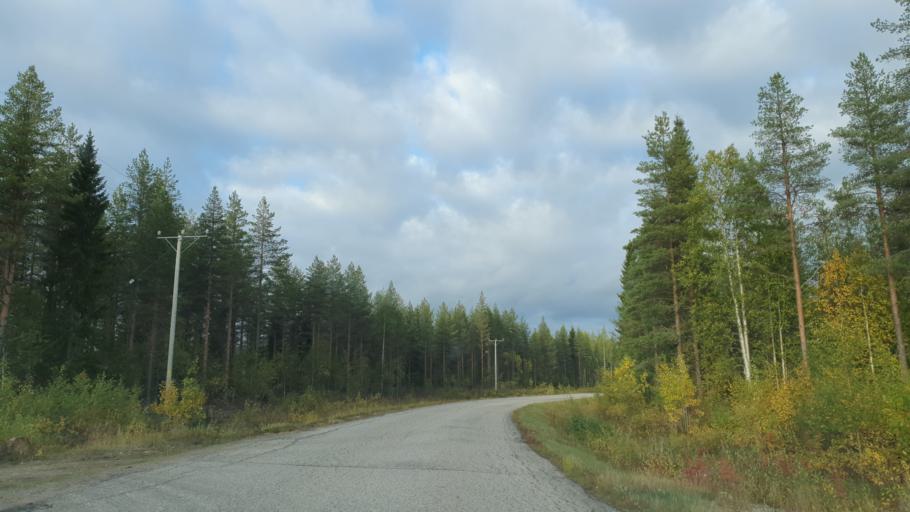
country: FI
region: North Karelia
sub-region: Pielisen Karjala
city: Lieksa
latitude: 63.9174
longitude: 30.1170
